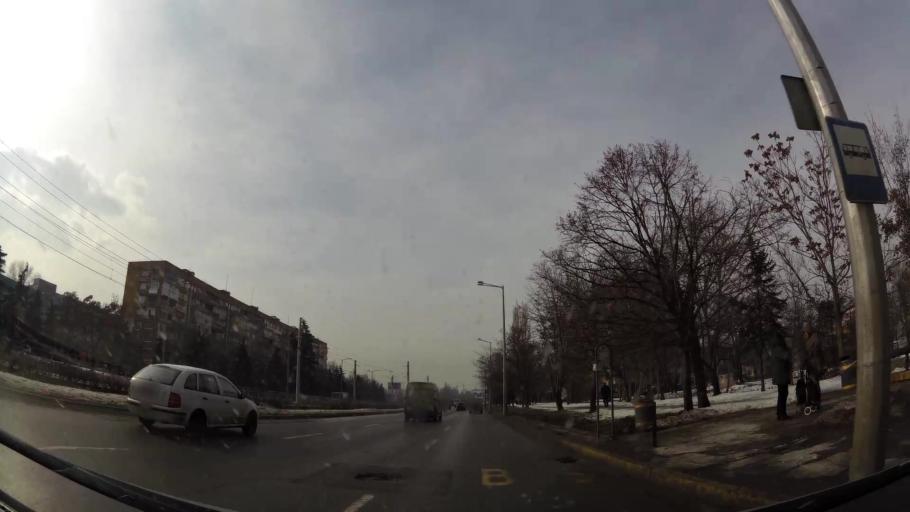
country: BG
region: Sofia-Capital
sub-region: Stolichna Obshtina
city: Sofia
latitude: 42.6993
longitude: 23.3649
